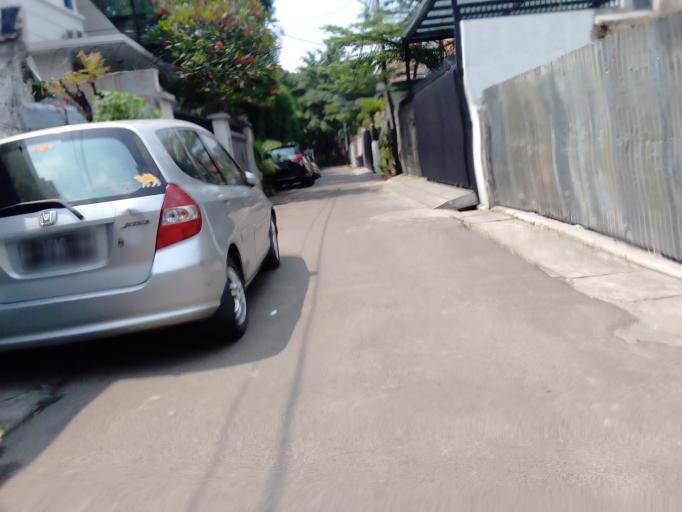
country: ID
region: Jakarta Raya
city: Jakarta
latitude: -6.2284
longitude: 106.8123
